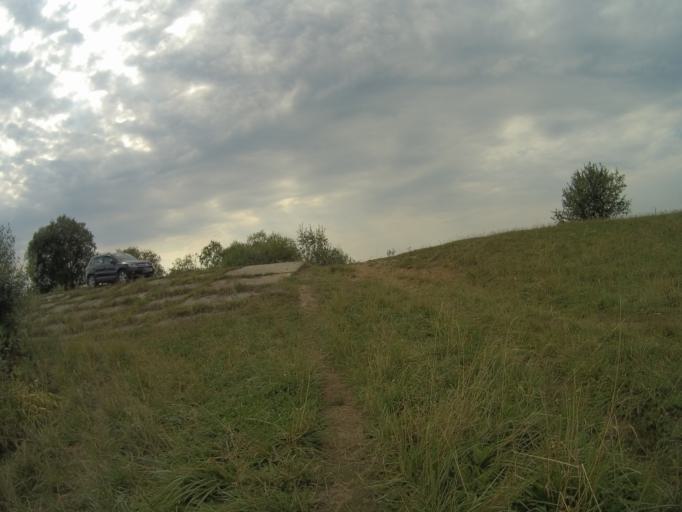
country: RU
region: Vladimir
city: Orgtrud
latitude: 56.0420
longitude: 40.6816
